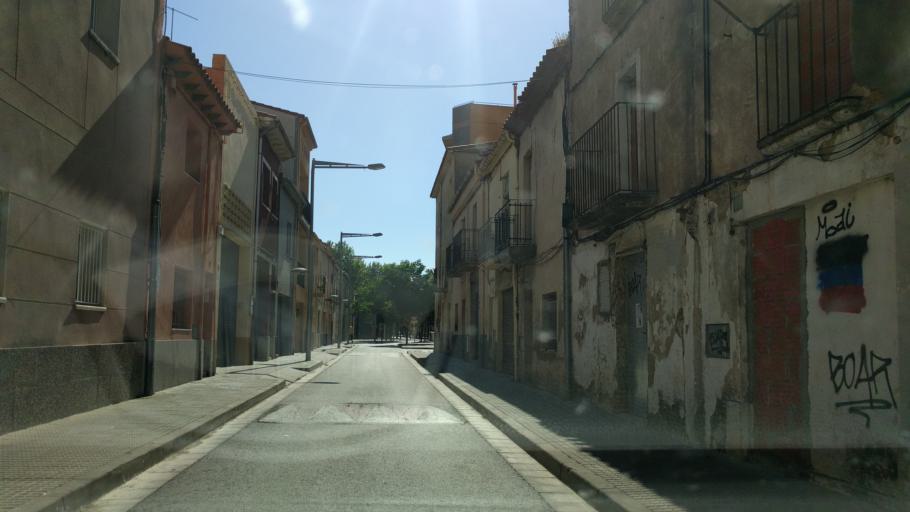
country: ES
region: Catalonia
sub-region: Provincia de Girona
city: Salt
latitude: 41.9776
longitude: 2.7984
